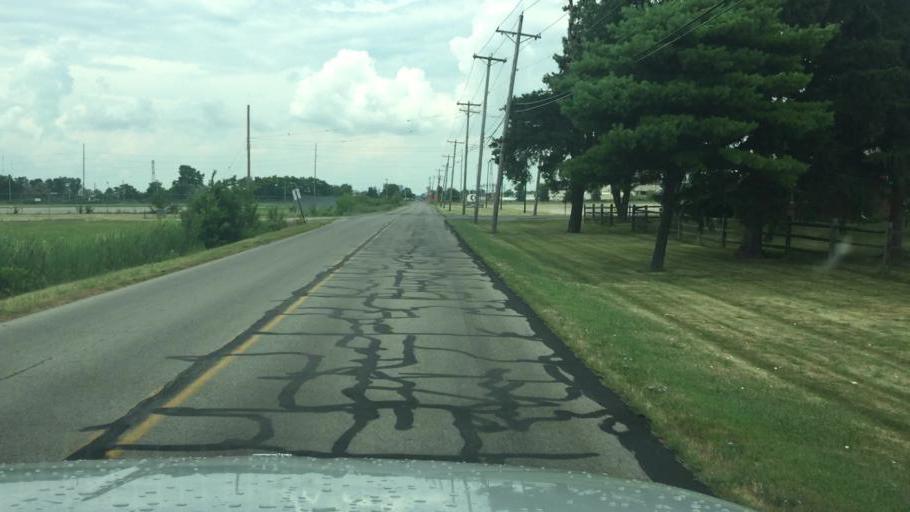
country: US
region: Ohio
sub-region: Wood County
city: Walbridge
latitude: 41.5873
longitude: -83.5275
